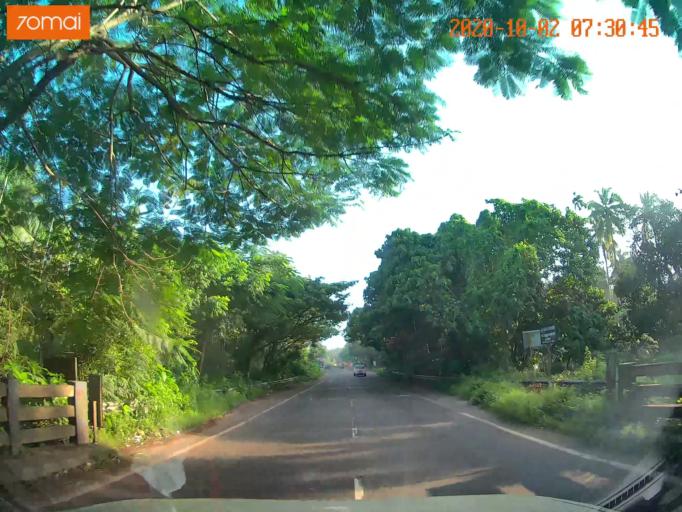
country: IN
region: Kerala
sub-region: Malappuram
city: Pariyapuram
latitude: 11.0438
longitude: 75.9400
